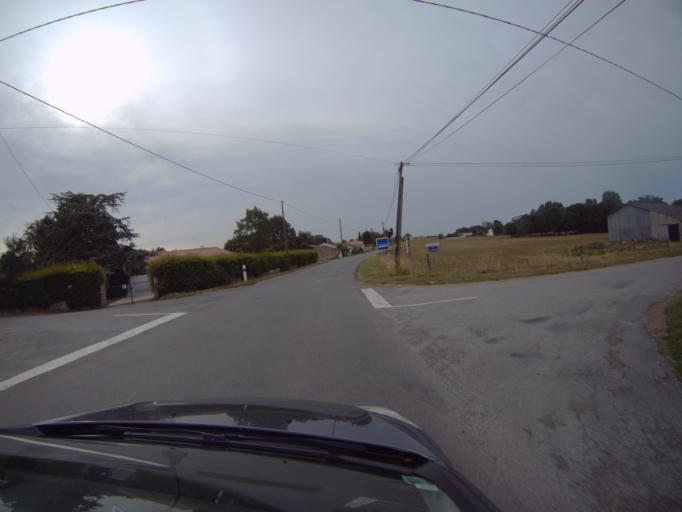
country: FR
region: Pays de la Loire
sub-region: Departement de la Vendee
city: Longeville-sur-Mer
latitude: 46.4151
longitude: -1.4546
